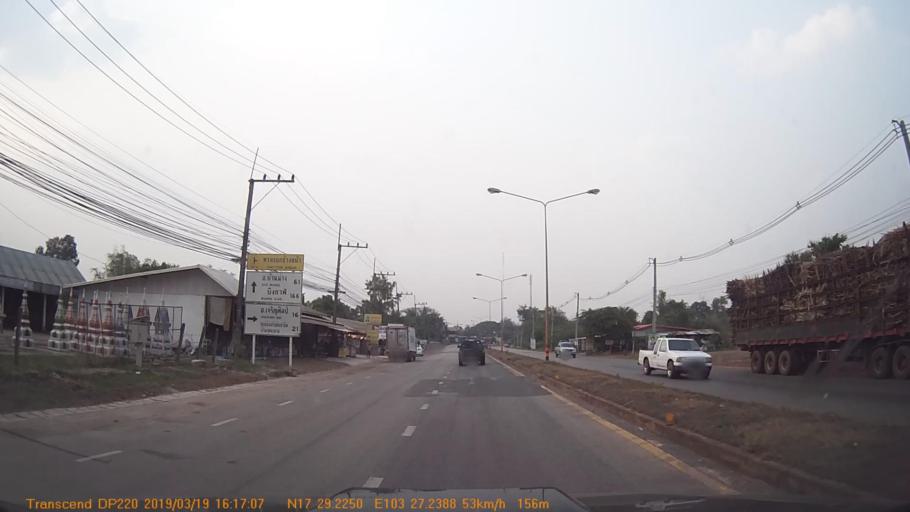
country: TH
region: Sakon Nakhon
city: Sawang Daen Din
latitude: 17.4875
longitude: 103.4538
